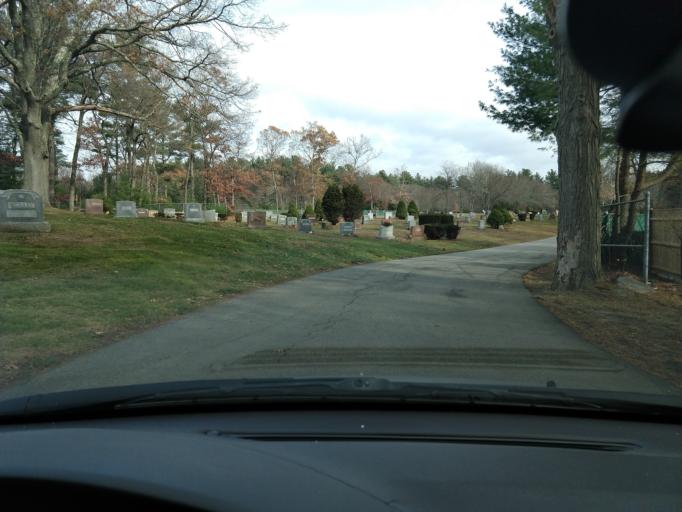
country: US
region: Massachusetts
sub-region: Middlesex County
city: Bedford
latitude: 42.4858
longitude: -71.2557
